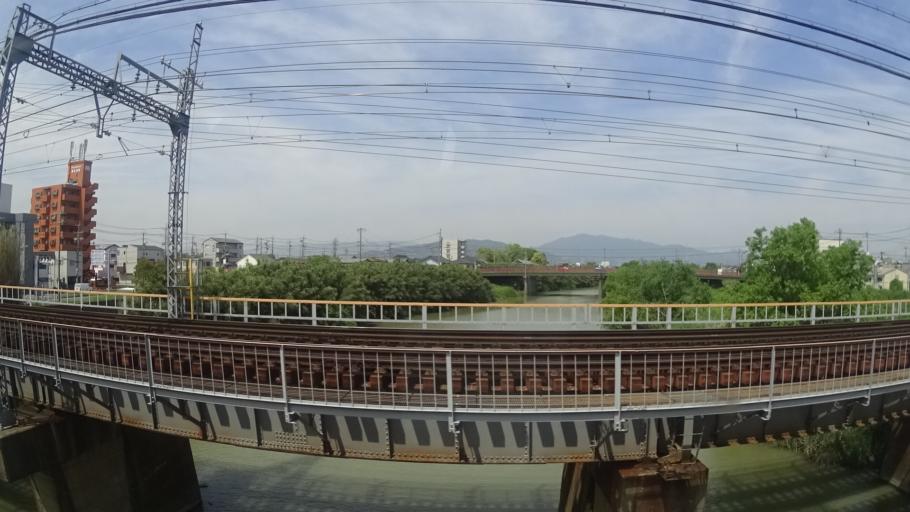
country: JP
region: Mie
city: Tsu-shi
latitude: 34.7215
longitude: 136.5017
